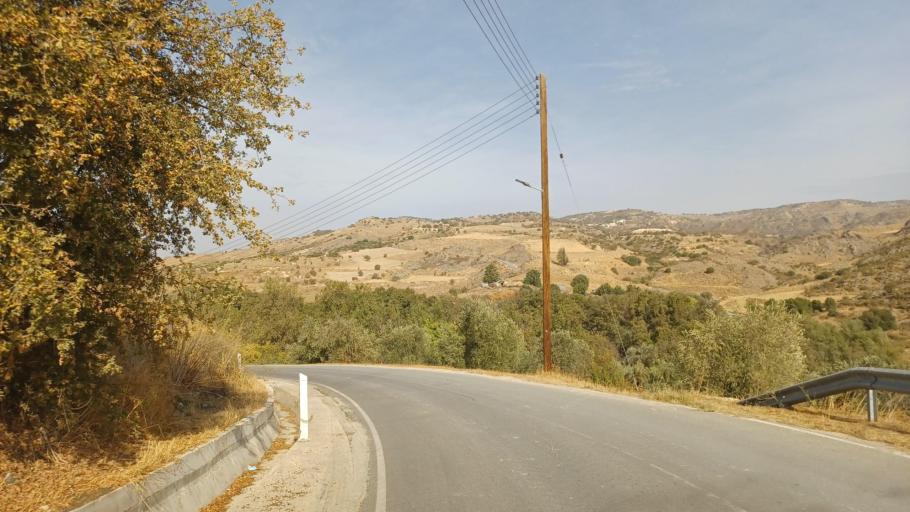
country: CY
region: Pafos
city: Polis
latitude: 34.9546
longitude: 32.5116
